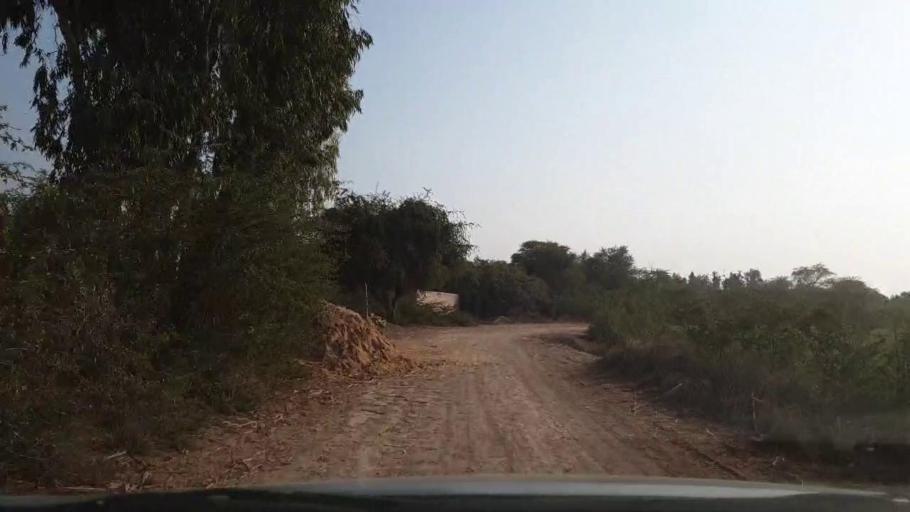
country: PK
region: Sindh
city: Tando Adam
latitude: 25.6656
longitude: 68.6489
